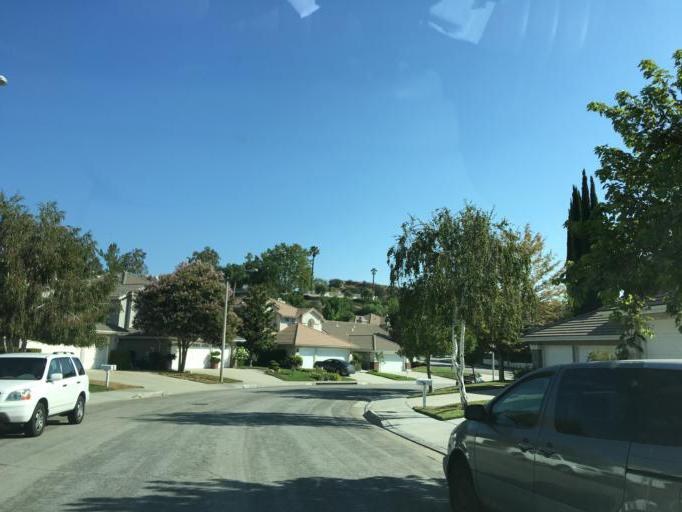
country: US
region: California
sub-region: Los Angeles County
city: Santa Clarita
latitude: 34.3861
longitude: -118.5866
